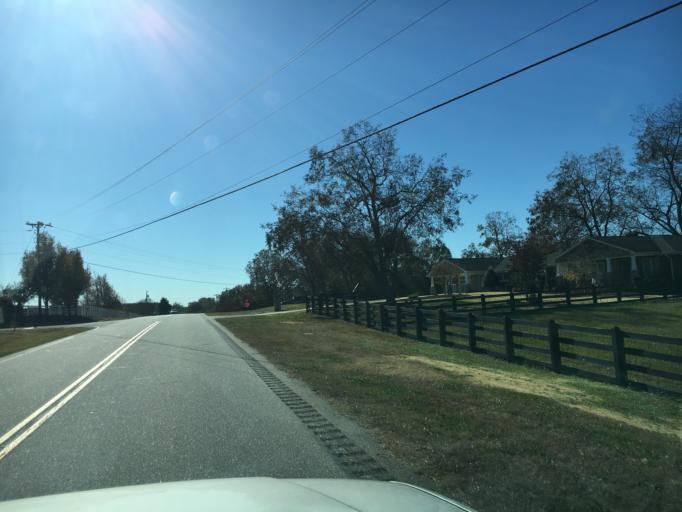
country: US
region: South Carolina
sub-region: Anderson County
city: Centerville
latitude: 34.4877
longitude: -82.7824
